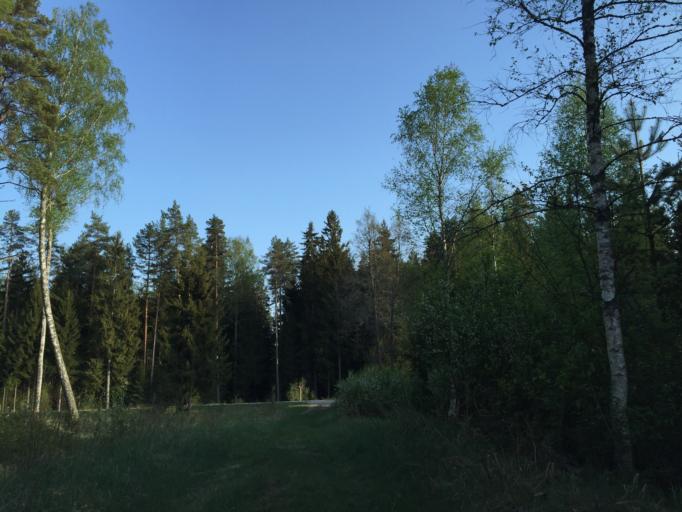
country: LV
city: Tireli
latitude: 56.8379
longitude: 23.7074
